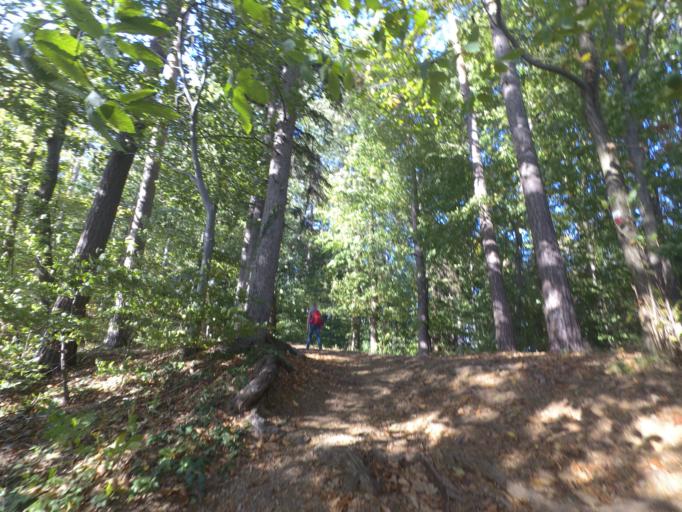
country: AT
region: Styria
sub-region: Politischer Bezirk Leibnitz
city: Kitzeck im Sausal
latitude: 46.7818
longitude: 15.4331
